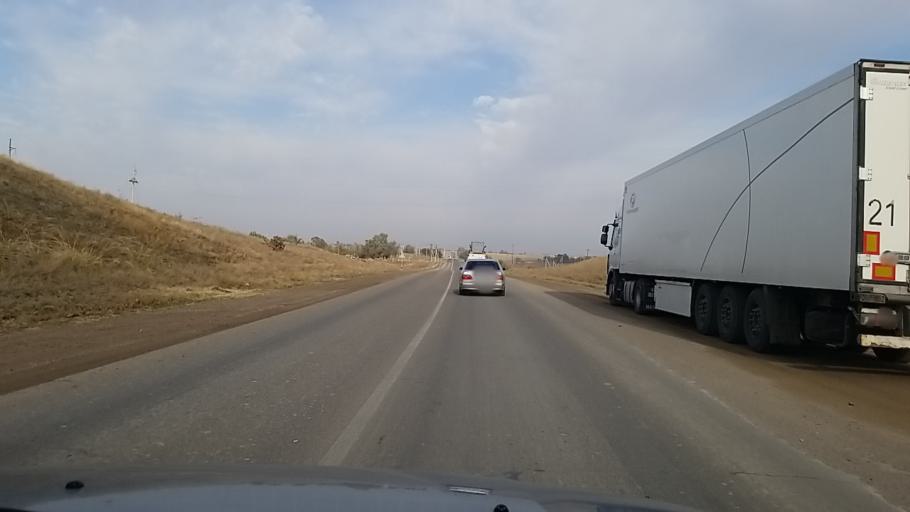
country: KZ
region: Almaty Oblysy
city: Burunday
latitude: 43.4654
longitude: 76.7059
